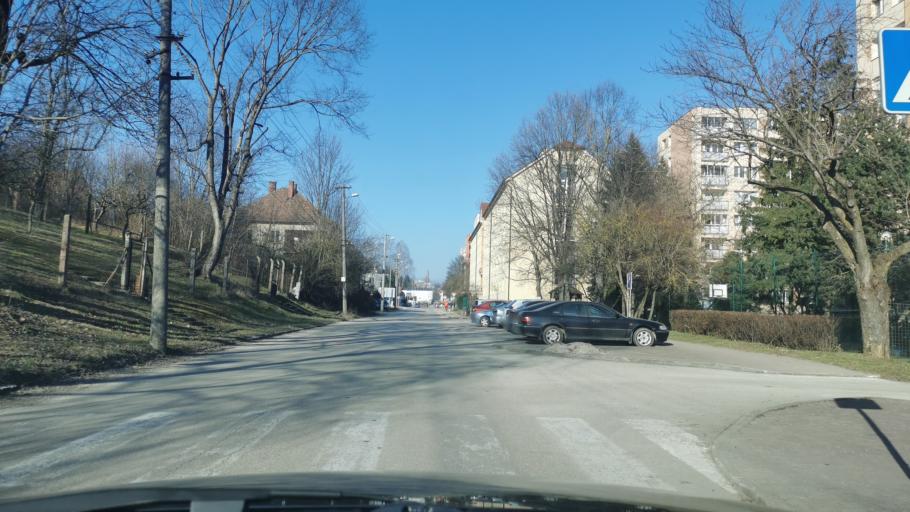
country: SK
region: Trenciansky
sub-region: Okres Myjava
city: Myjava
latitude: 48.7496
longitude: 17.5632
